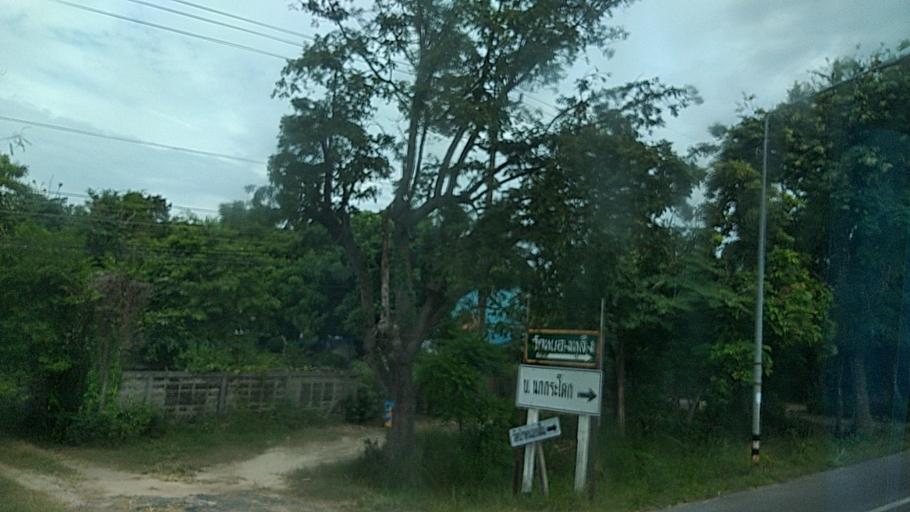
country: TH
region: Maha Sarakham
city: Maha Sarakham
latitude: 16.1496
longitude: 103.3923
